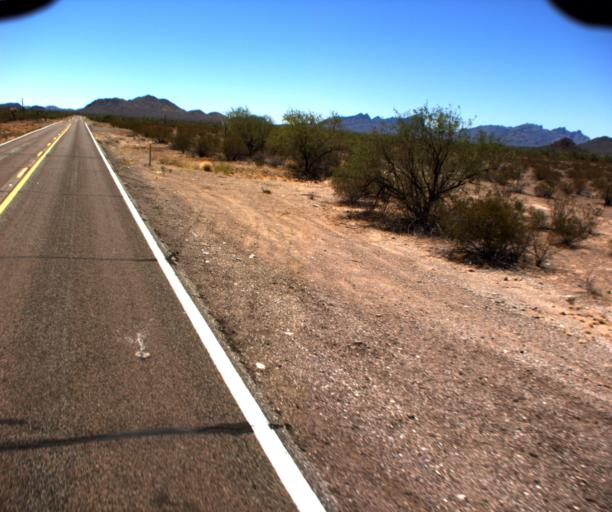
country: US
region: Arizona
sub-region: Pima County
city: Ajo
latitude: 32.2357
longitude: -112.7182
